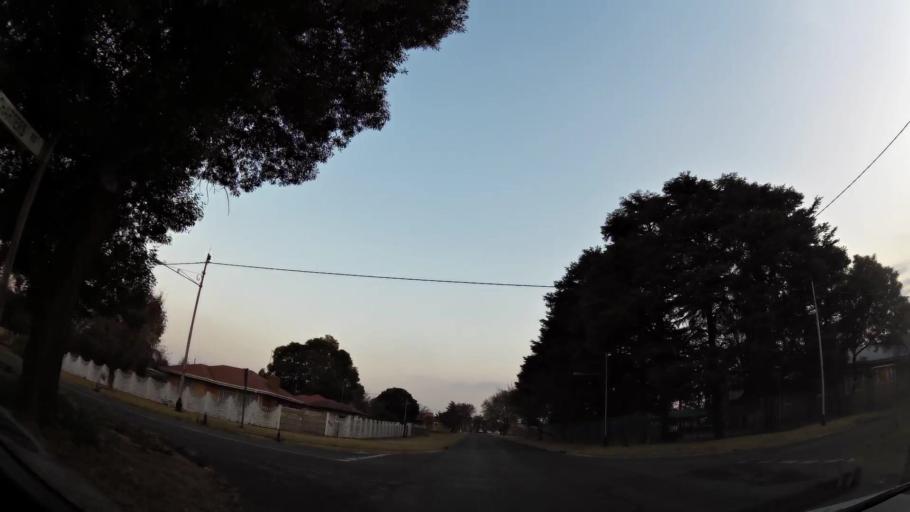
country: ZA
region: Gauteng
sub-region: Ekurhuleni Metropolitan Municipality
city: Nigel
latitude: -26.3511
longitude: 28.4396
